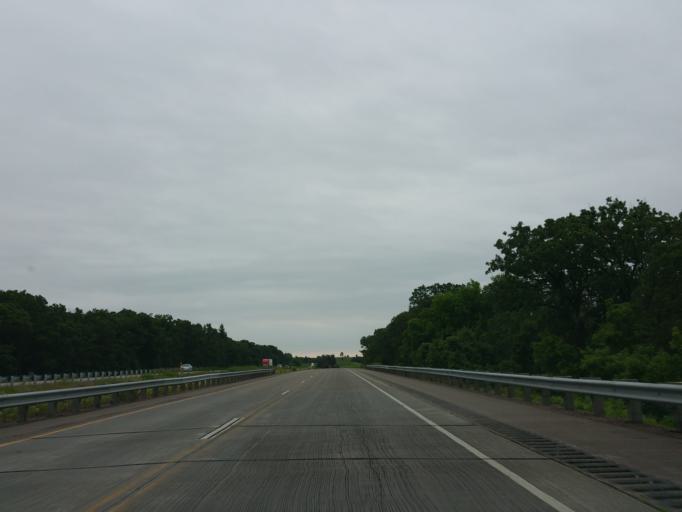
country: US
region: Wisconsin
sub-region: Eau Claire County
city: Fall Creek
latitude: 44.6793
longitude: -91.3266
